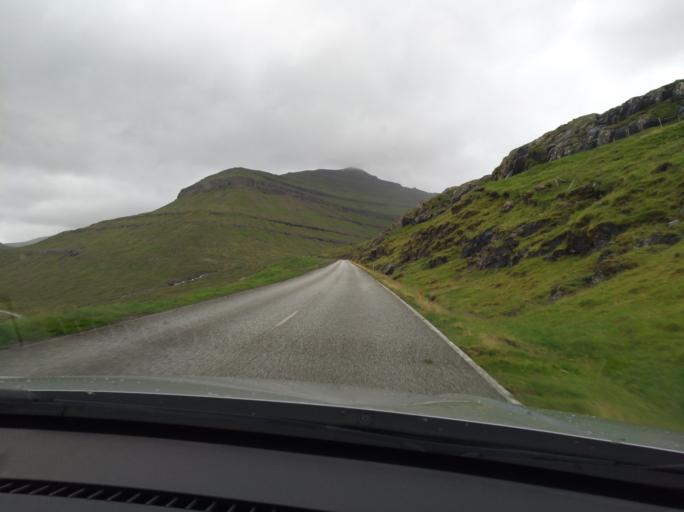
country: FO
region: Eysturoy
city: Fuglafjordur
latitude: 62.2187
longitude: -6.8673
